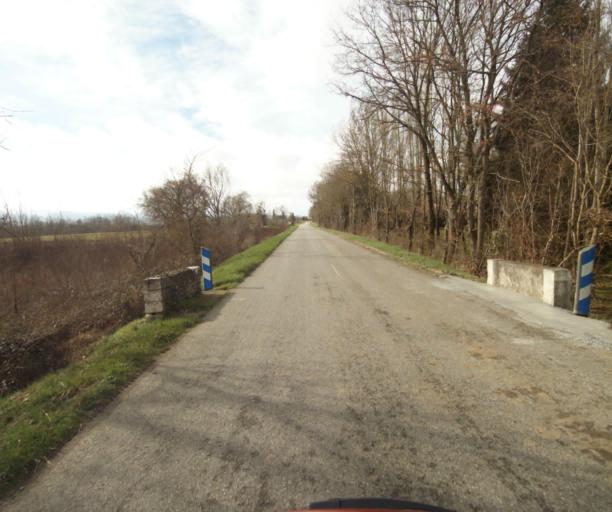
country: FR
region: Midi-Pyrenees
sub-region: Departement de l'Ariege
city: Pamiers
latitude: 43.1319
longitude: 1.5553
